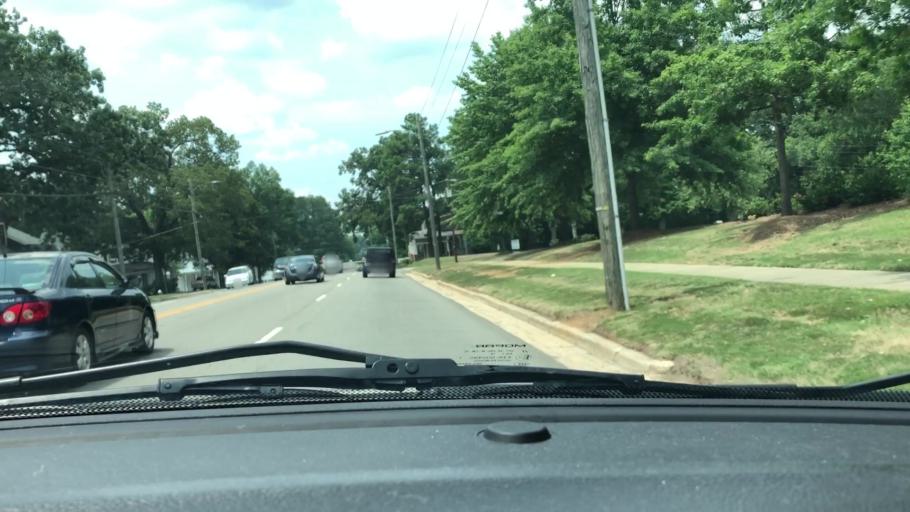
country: US
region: North Carolina
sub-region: Lee County
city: Sanford
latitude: 35.4819
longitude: -79.1822
